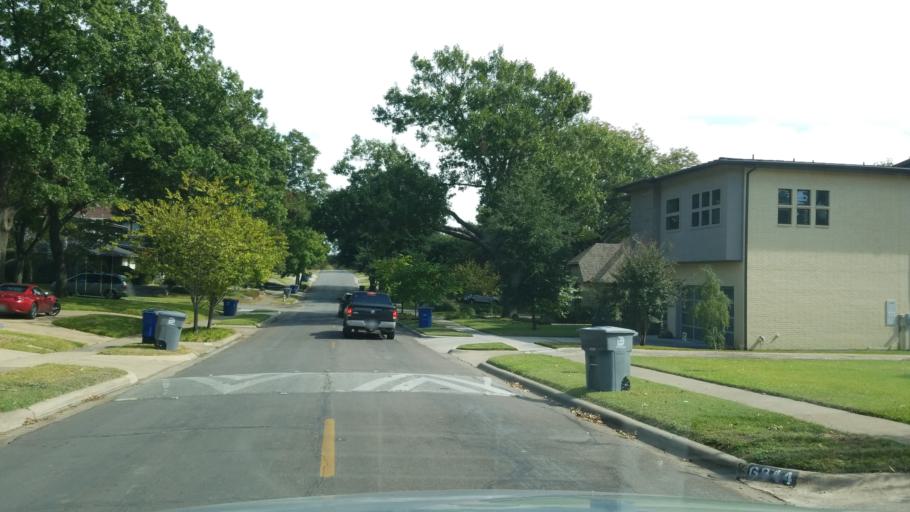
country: US
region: Texas
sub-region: Dallas County
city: Highland Park
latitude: 32.8115
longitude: -96.7421
